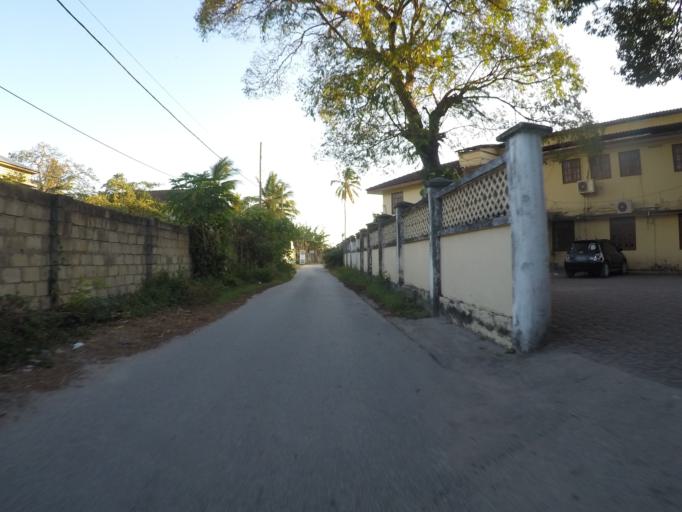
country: TZ
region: Zanzibar Urban/West
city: Zanzibar
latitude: -6.1748
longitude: 39.1986
